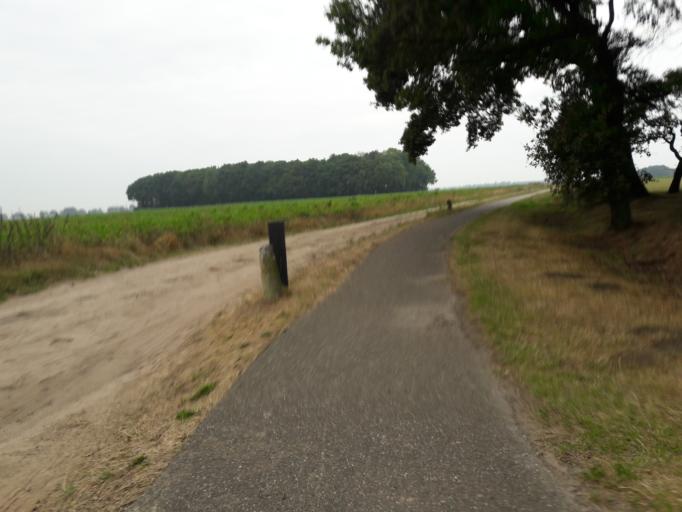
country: NL
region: Drenthe
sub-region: Gemeente Borger-Odoorn
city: Borger
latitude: 52.9442
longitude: 6.8007
